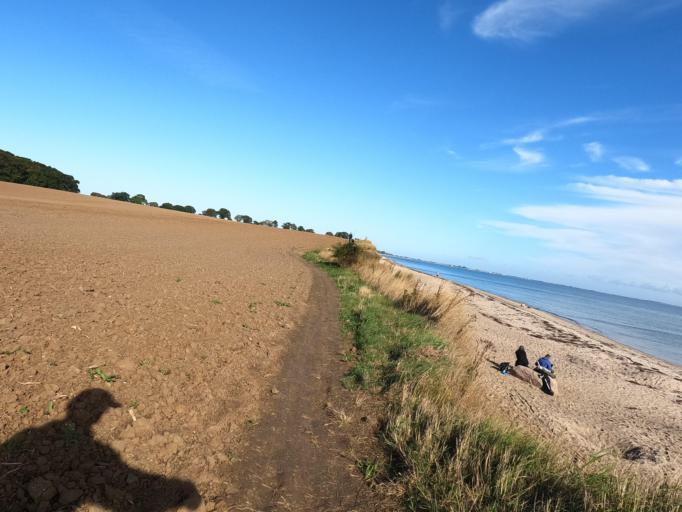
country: DE
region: Schleswig-Holstein
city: Dahme
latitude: 54.2827
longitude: 11.0825
